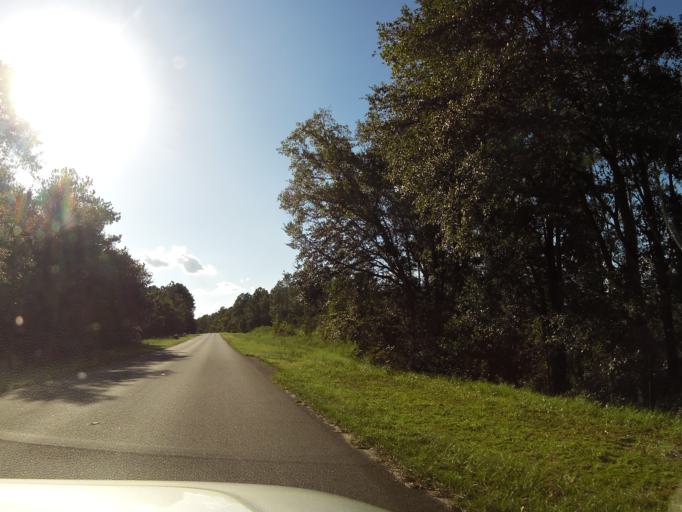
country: US
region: Florida
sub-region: Wakulla County
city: Crawfordville
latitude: 30.0637
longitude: -84.5062
